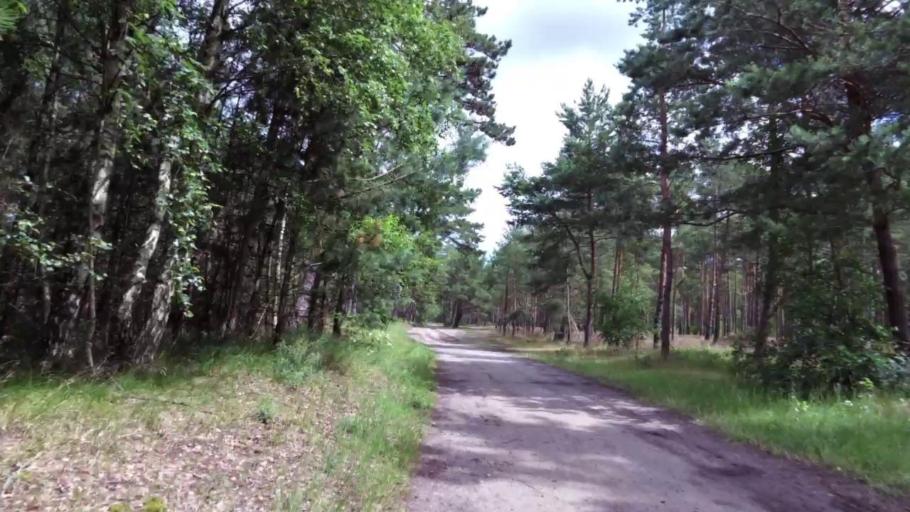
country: PL
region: West Pomeranian Voivodeship
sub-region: Powiat slawienski
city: Darlowo
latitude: 54.4998
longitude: 16.4540
